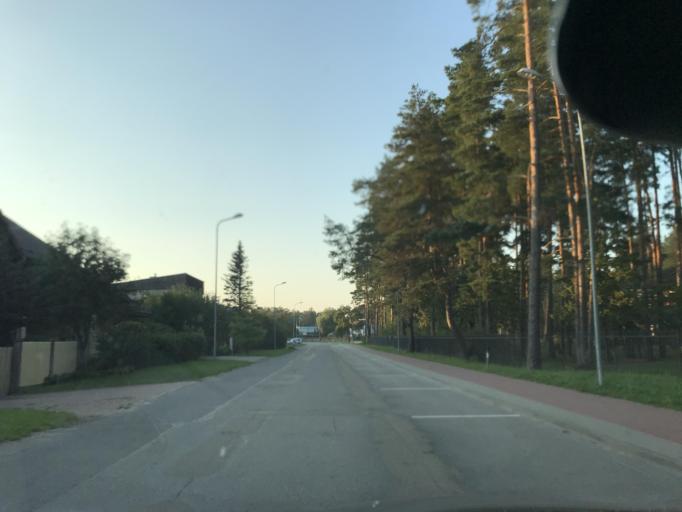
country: LV
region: Ikskile
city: Ikskile
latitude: 56.8298
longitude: 24.5048
